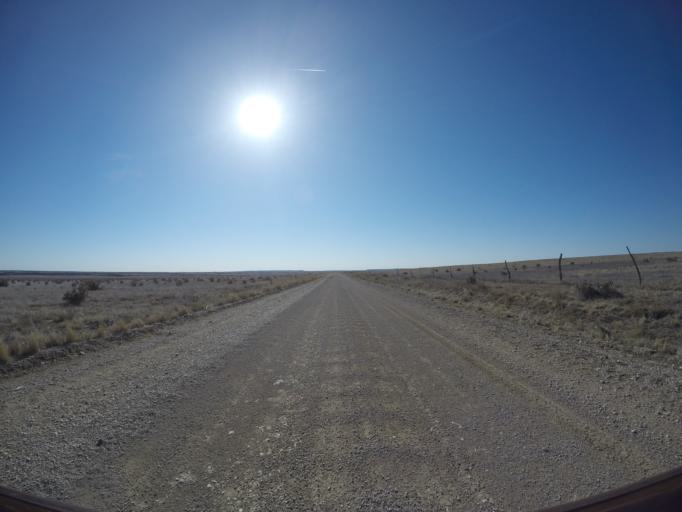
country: US
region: Colorado
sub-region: Otero County
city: La Junta
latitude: 37.7350
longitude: -103.6207
